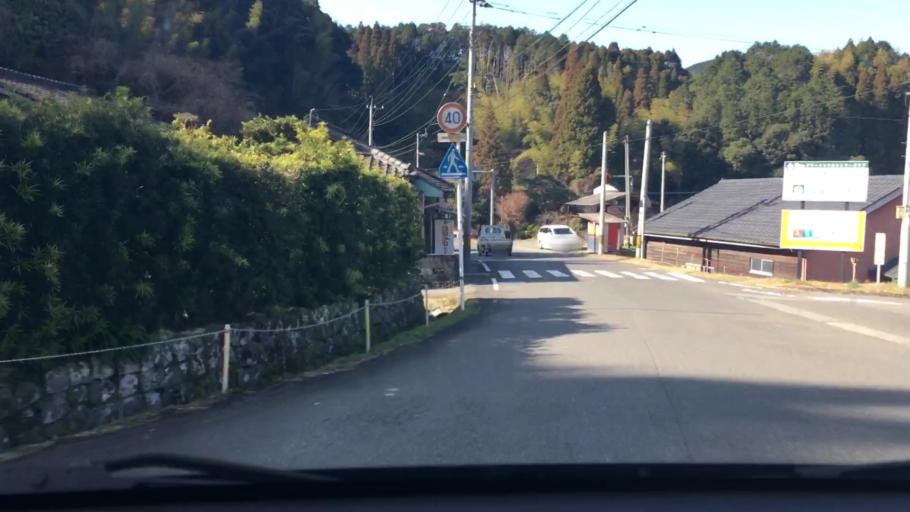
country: JP
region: Kagoshima
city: Ijuin
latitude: 31.7359
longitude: 130.4135
